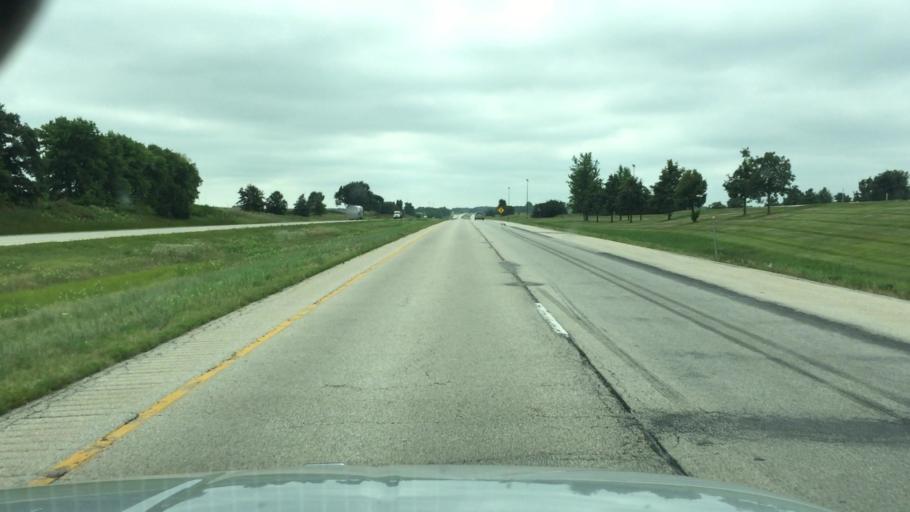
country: US
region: Illinois
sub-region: Henry County
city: Orion
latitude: 41.2340
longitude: -90.3320
